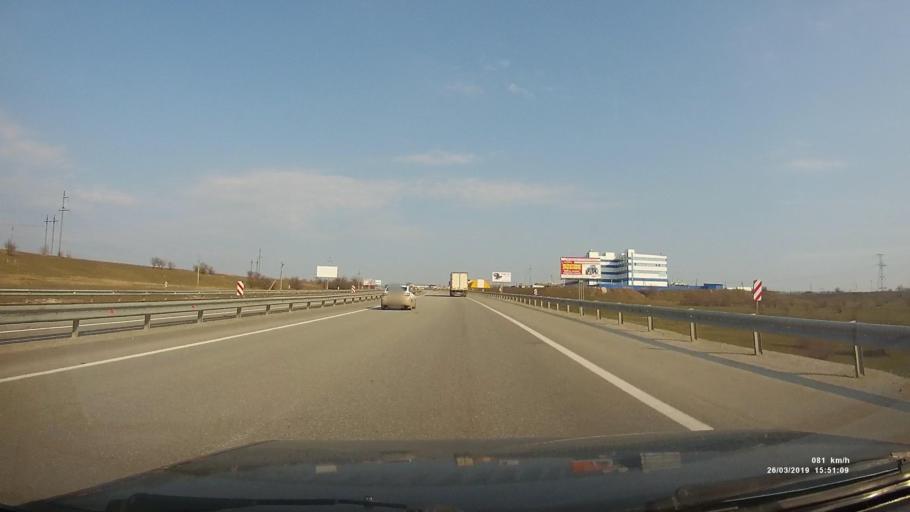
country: RU
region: Rostov
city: Chaltyr
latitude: 47.2702
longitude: 39.4992
